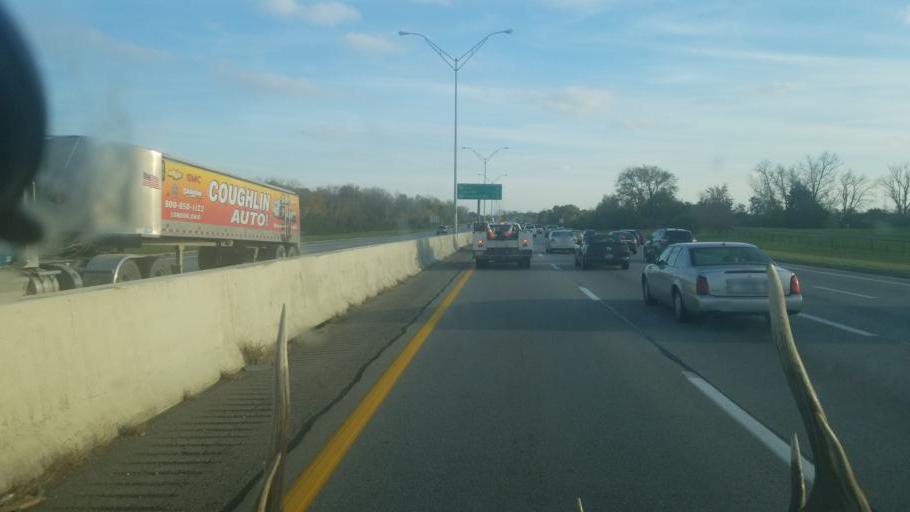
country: US
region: Ohio
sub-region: Franklin County
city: Bexley
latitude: 39.9413
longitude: -82.9396
